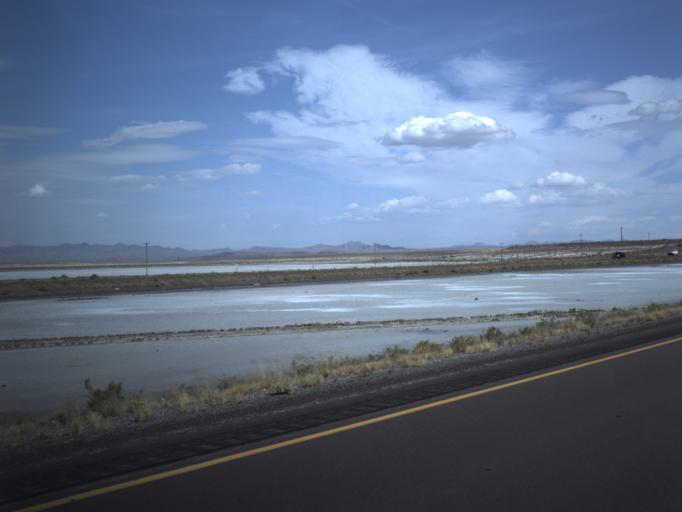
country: US
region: Utah
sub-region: Tooele County
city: Wendover
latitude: 40.7265
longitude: -113.2668
